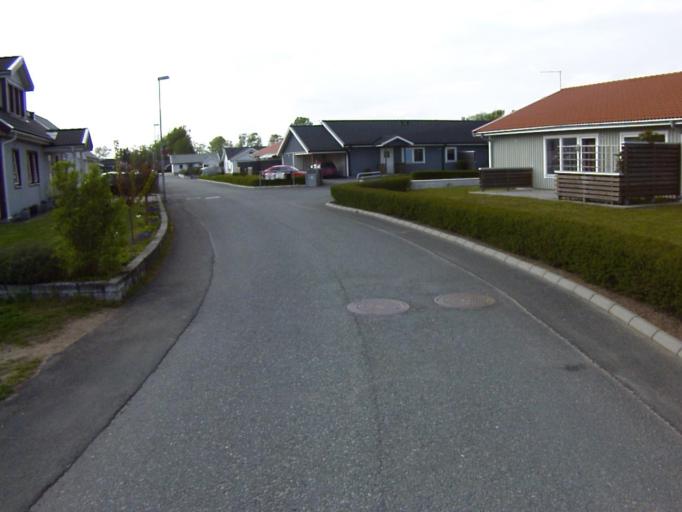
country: SE
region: Skane
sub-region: Kristianstads Kommun
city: Fjalkinge
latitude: 56.0454
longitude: 14.2777
